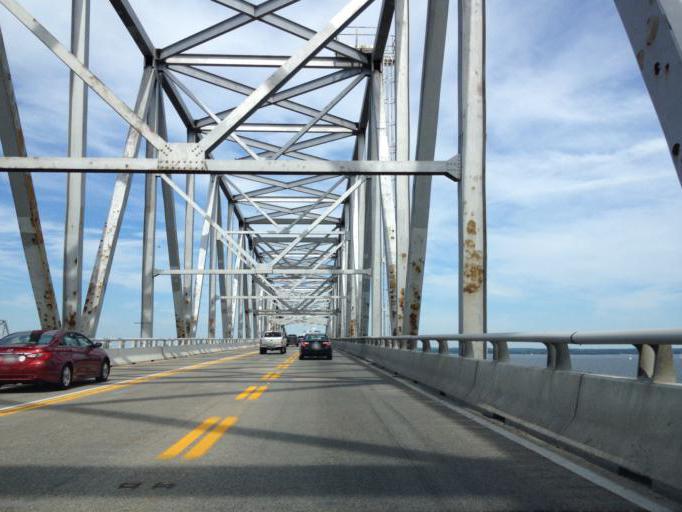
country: US
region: Maryland
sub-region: Queen Anne's County
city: Stevensville
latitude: 38.9889
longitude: -76.3577
